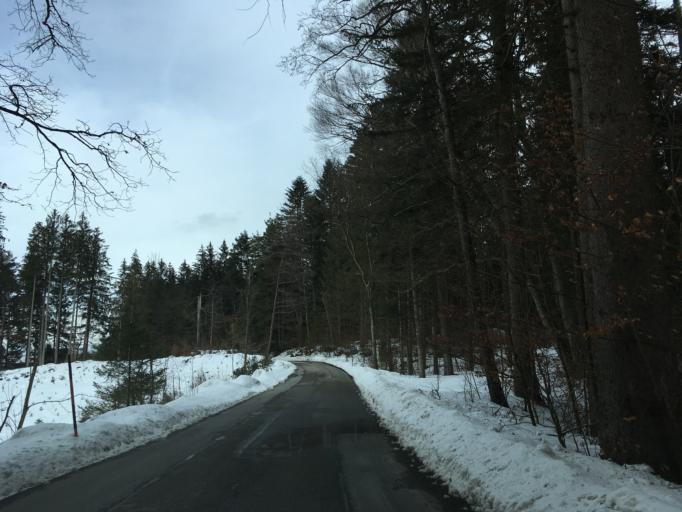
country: DE
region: Bavaria
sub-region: Upper Bavaria
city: Schnaitsee
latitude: 48.0433
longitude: 12.3609
